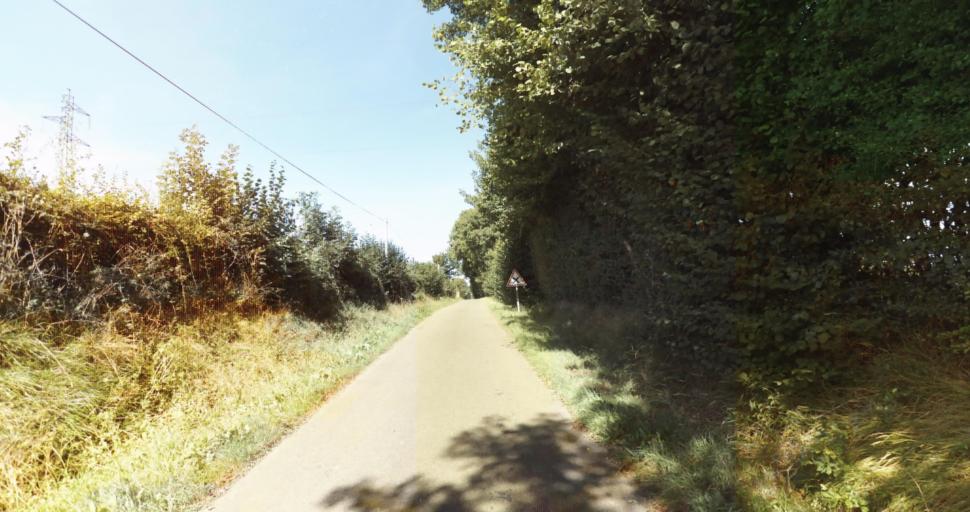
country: FR
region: Lower Normandy
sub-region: Departement de l'Orne
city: Gace
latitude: 48.7616
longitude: 0.2684
